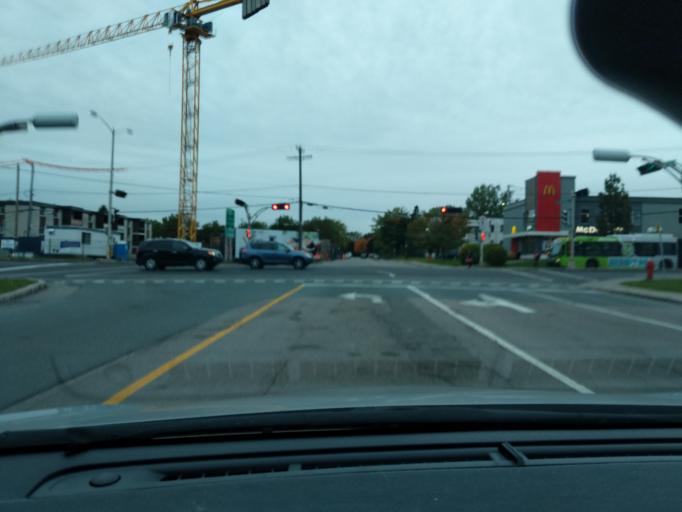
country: CA
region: Quebec
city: L'Ancienne-Lorette
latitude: 46.7663
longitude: -71.3111
